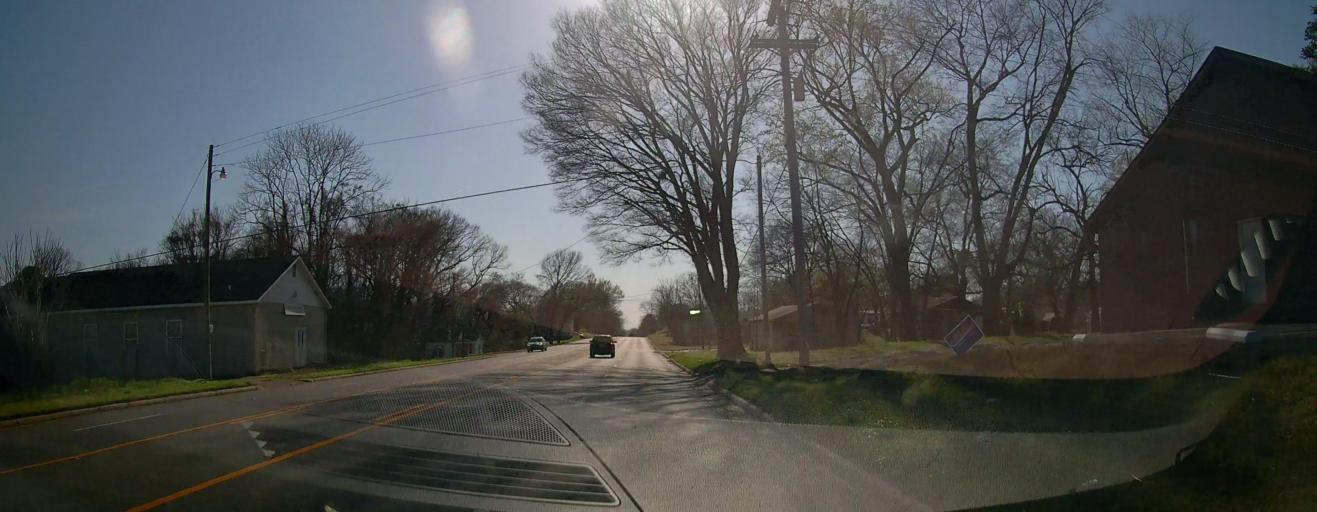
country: US
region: Alabama
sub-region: Lauderdale County
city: East Florence
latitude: 34.8083
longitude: -87.6395
